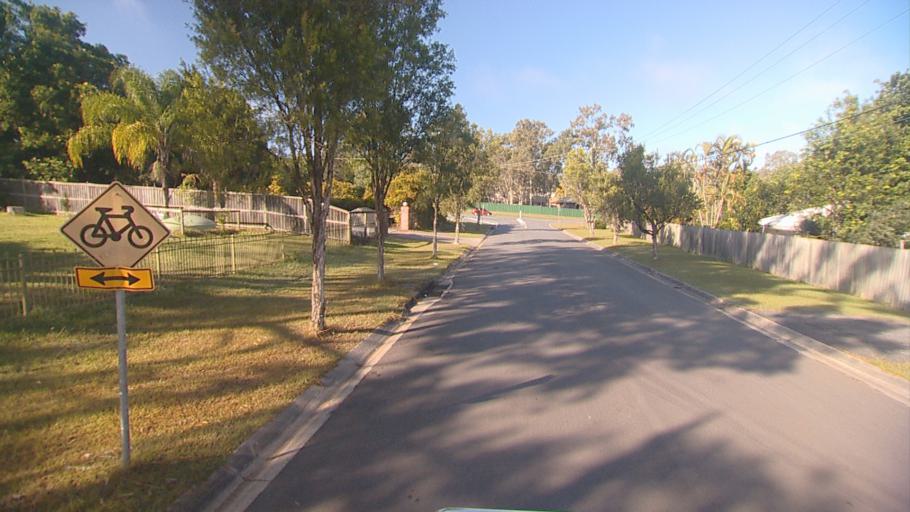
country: AU
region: Queensland
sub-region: Logan
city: Park Ridge South
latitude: -27.6980
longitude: 153.0324
